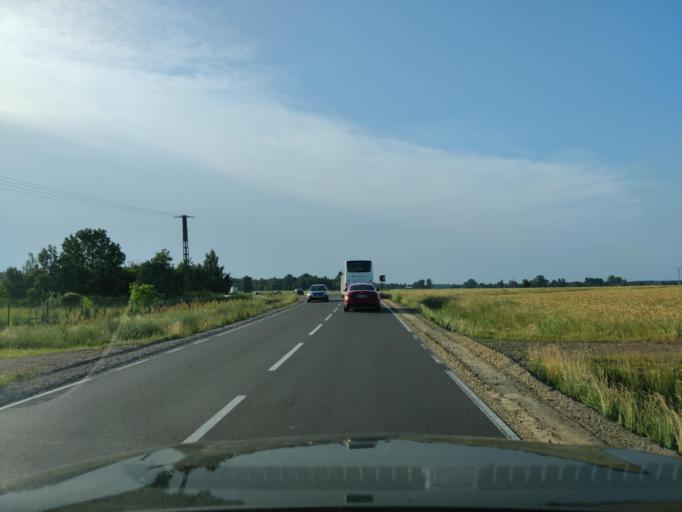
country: PL
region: Masovian Voivodeship
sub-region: Powiat plonski
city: Baboszewo
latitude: 52.7095
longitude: 20.3377
